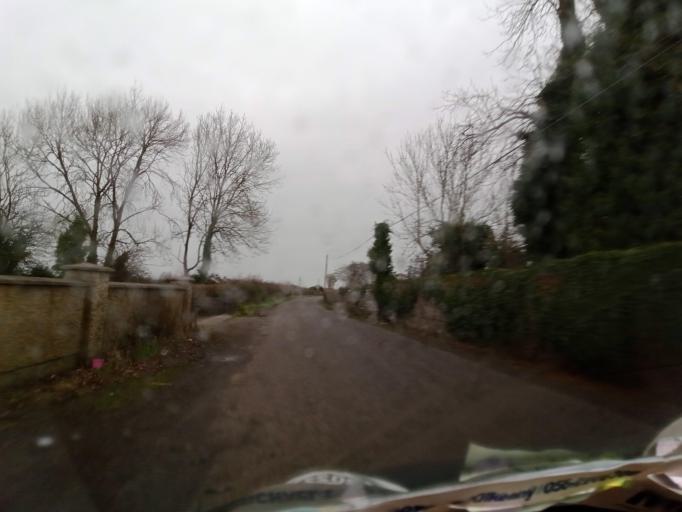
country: IE
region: Munster
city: Fethard
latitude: 52.5583
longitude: -7.7655
